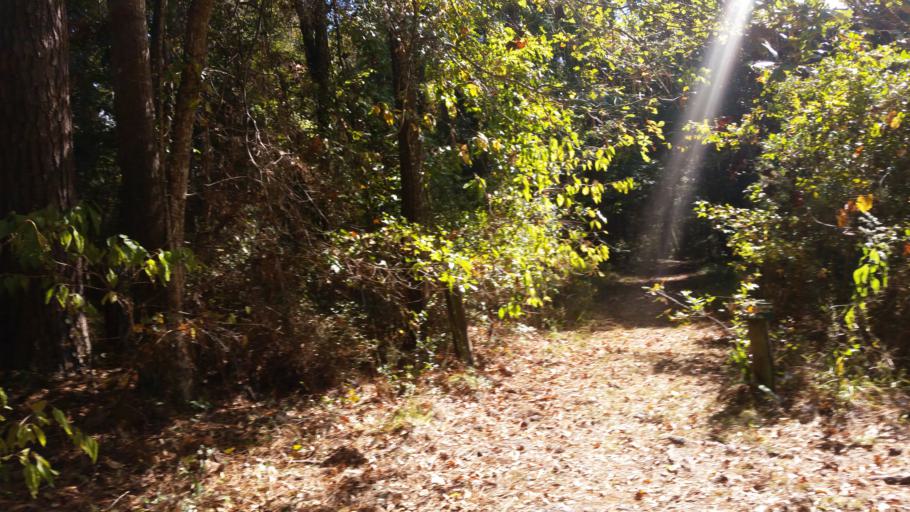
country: US
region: Alabama
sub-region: Baldwin County
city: Spanish Fort
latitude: 30.7421
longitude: -87.9228
